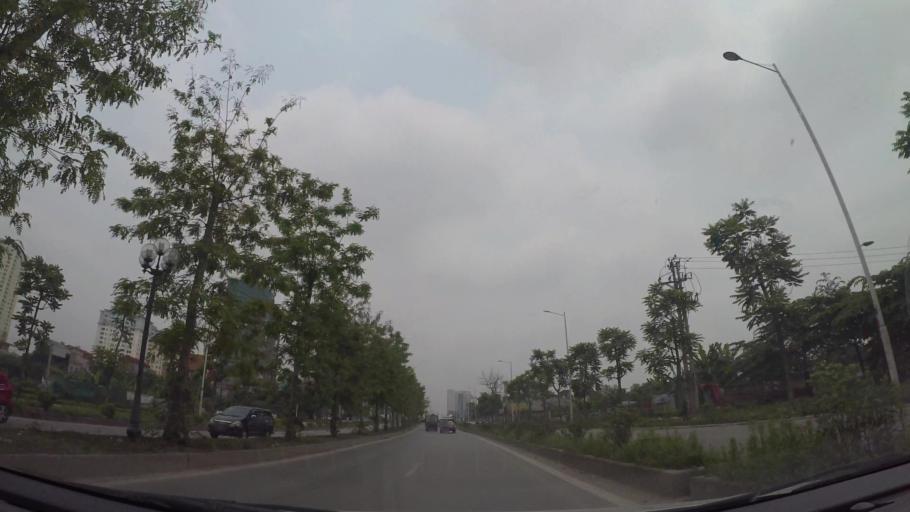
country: VN
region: Ha Noi
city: Cau Dien
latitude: 21.0314
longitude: 105.7569
